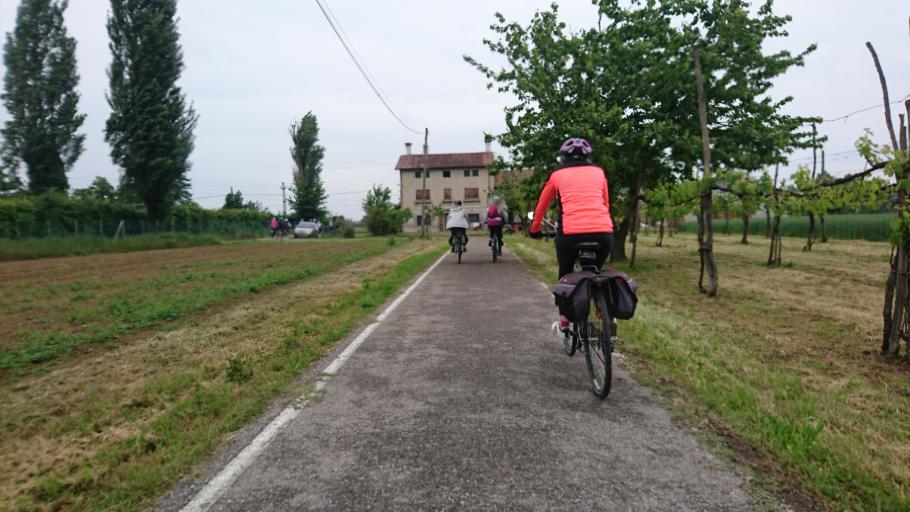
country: IT
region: Veneto
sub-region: Provincia di Padova
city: Montemerlo
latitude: 45.3895
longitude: 11.6906
